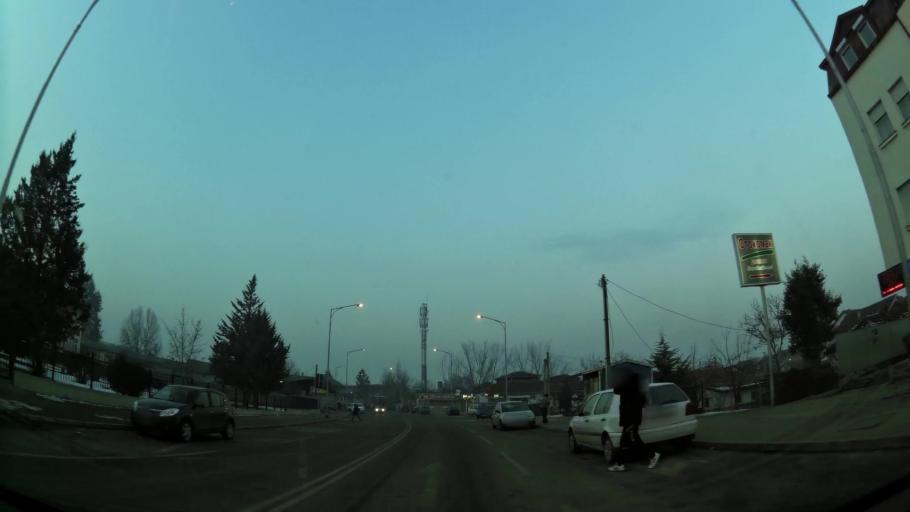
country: MK
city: Creshevo
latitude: 42.0037
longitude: 21.5040
